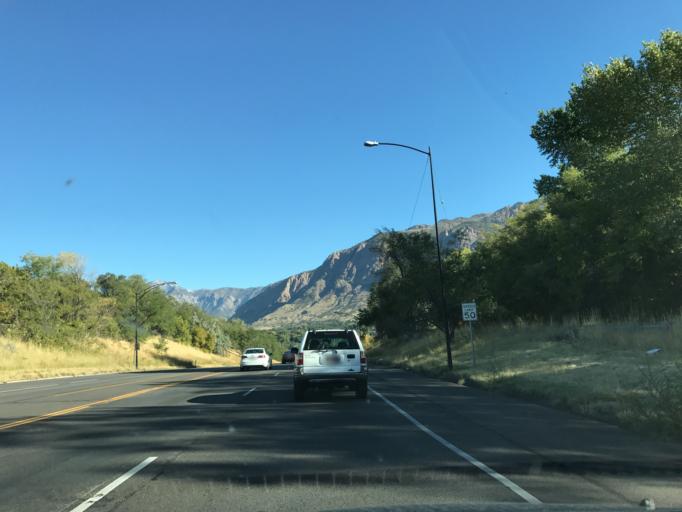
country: US
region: Utah
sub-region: Weber County
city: Ogden
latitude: 41.2314
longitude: -111.9477
